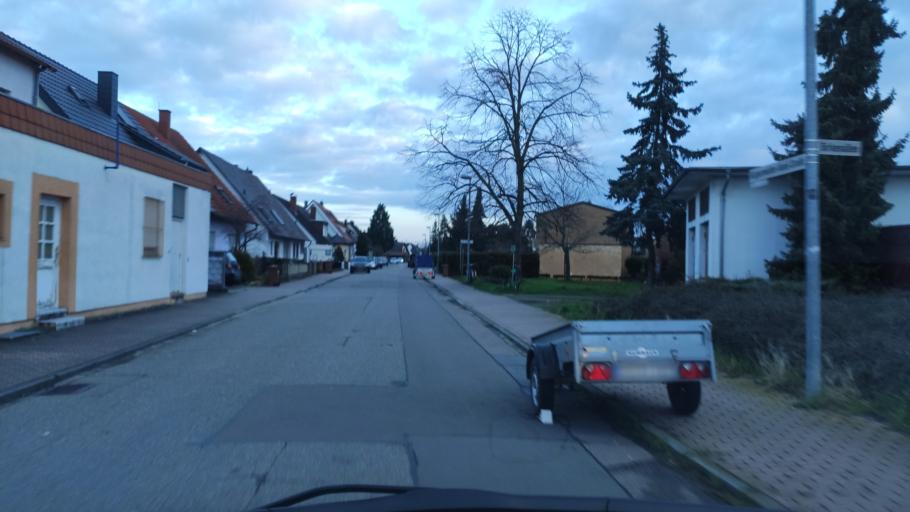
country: DE
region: Baden-Wuerttemberg
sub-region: Karlsruhe Region
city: Hockenheim
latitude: 49.3251
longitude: 8.5541
